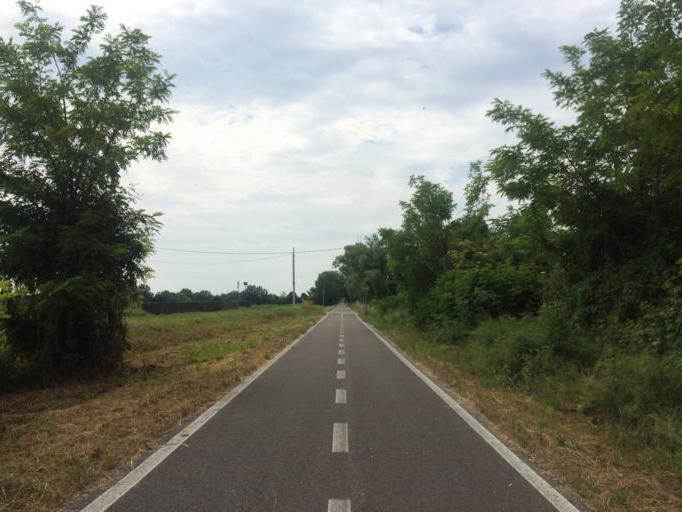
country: IT
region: Friuli Venezia Giulia
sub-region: Provincia di Udine
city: Aquileia
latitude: 45.7598
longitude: 13.3741
